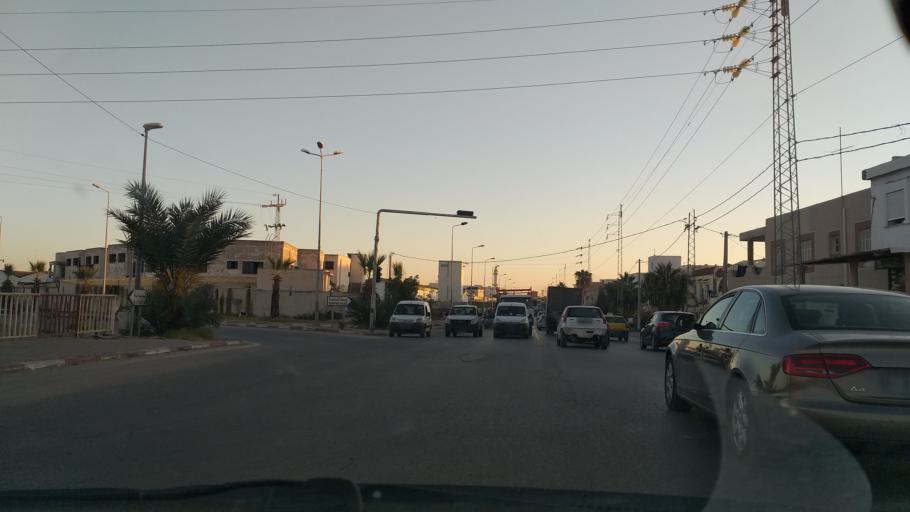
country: TN
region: Safaqis
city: Al Qarmadah
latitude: 34.7687
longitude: 10.7743
